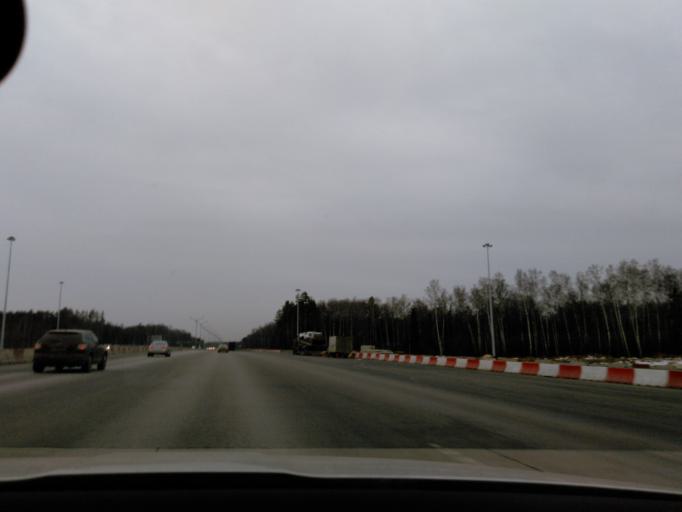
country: RU
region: Moscow
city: Khimki
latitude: 55.9351
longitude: 37.4507
